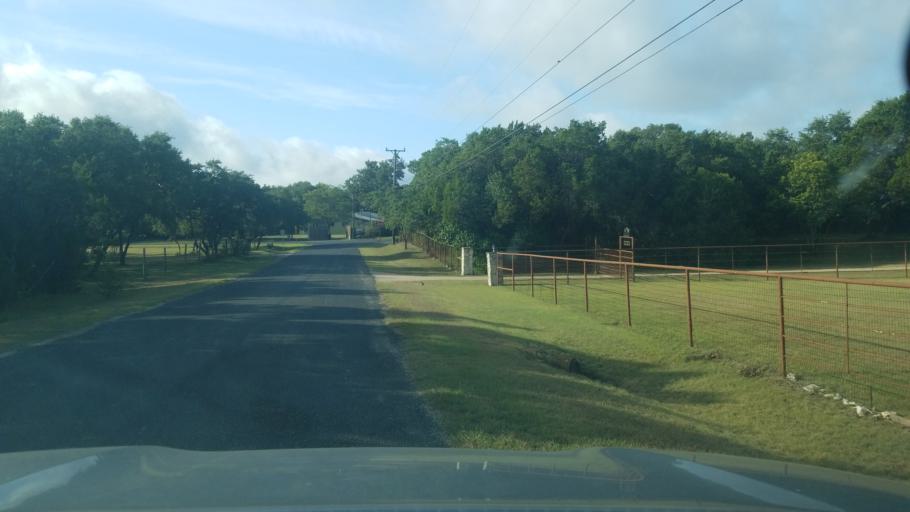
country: US
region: Texas
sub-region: Bexar County
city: Timberwood Park
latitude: 29.6959
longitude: -98.5152
